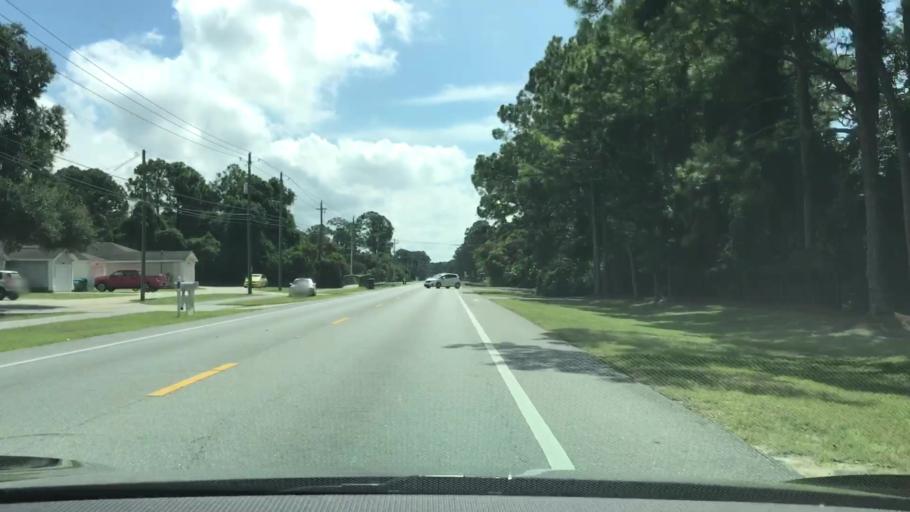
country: US
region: Florida
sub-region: Bay County
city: Panama City Beach
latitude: 30.1671
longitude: -85.7793
